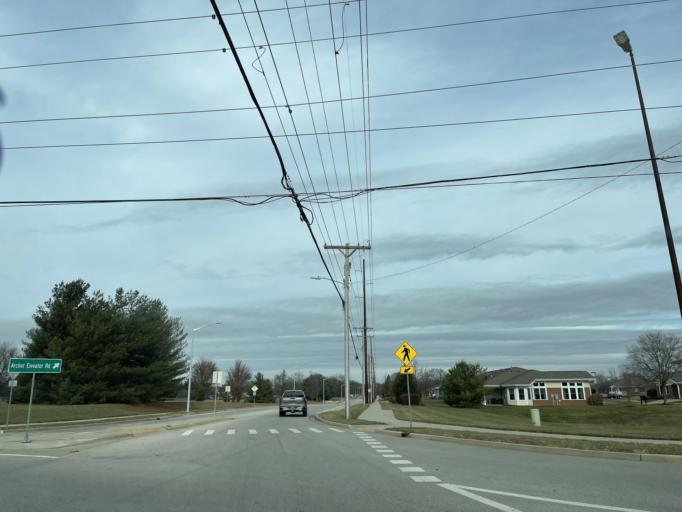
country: US
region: Illinois
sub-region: Sangamon County
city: Jerome
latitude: 39.7709
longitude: -89.7345
